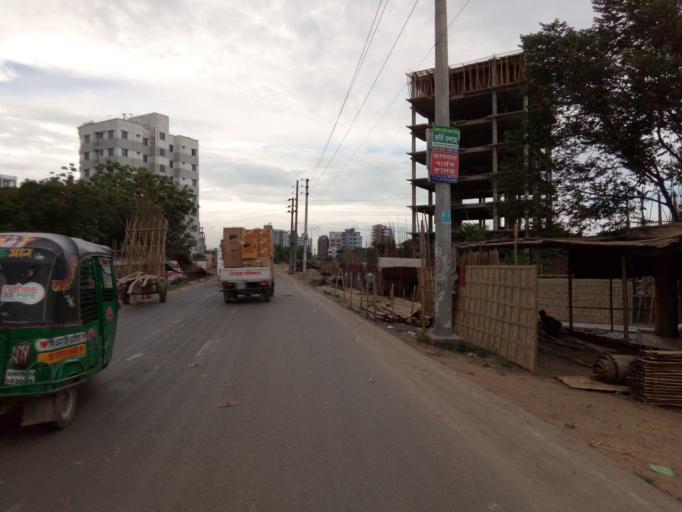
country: BD
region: Dhaka
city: Paltan
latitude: 23.7610
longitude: 90.4453
